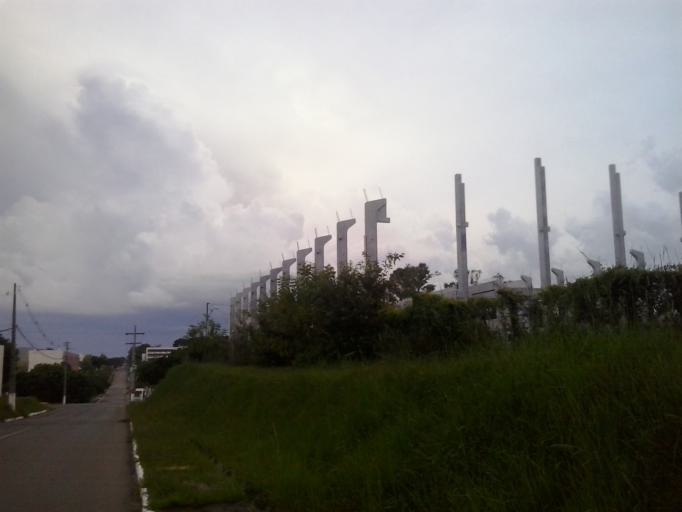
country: BR
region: Rio Grande do Sul
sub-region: Santa Maria
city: Santa Maria
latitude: -29.7148
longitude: -53.7188
